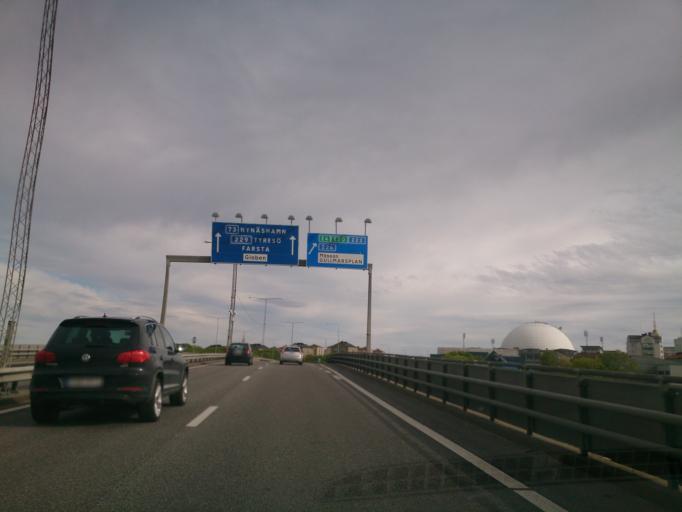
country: SE
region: Stockholm
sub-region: Stockholms Kommun
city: Arsta
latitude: 59.3023
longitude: 18.0784
